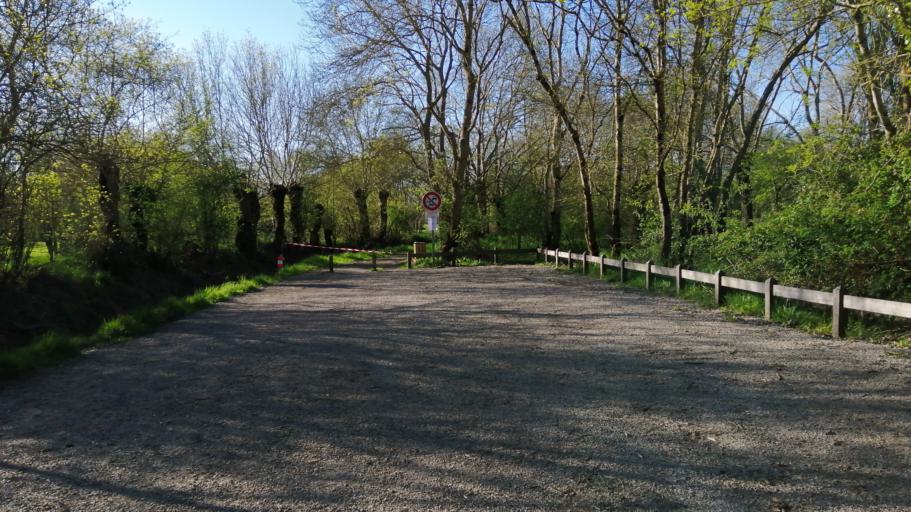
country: FR
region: Pays de la Loire
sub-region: Departement de la Loire-Atlantique
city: Saint-Gereon
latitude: 47.3577
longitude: -1.2014
